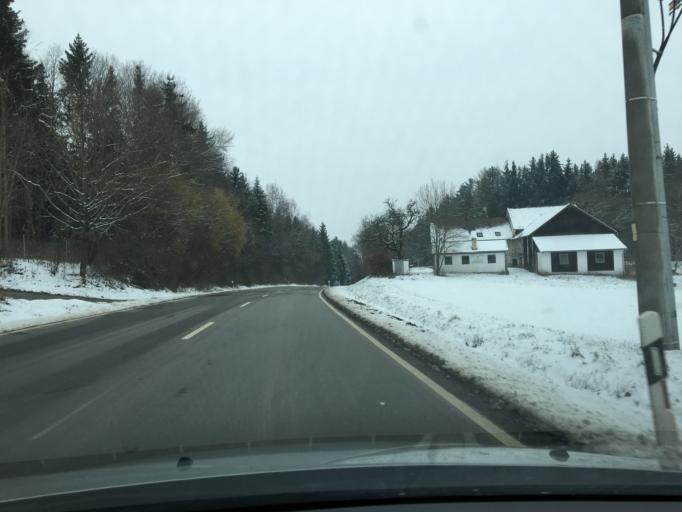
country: DE
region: Bavaria
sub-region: Lower Bavaria
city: Furth
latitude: 48.4344
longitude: 12.3808
